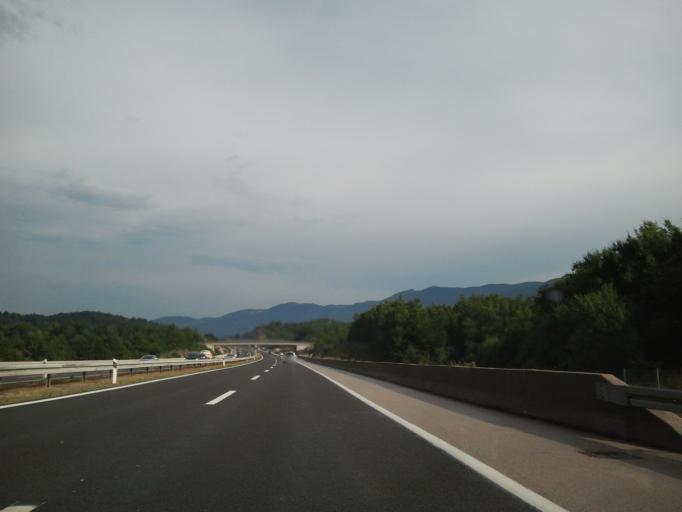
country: HR
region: Zadarska
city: Obrovac
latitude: 44.3436
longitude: 15.6468
